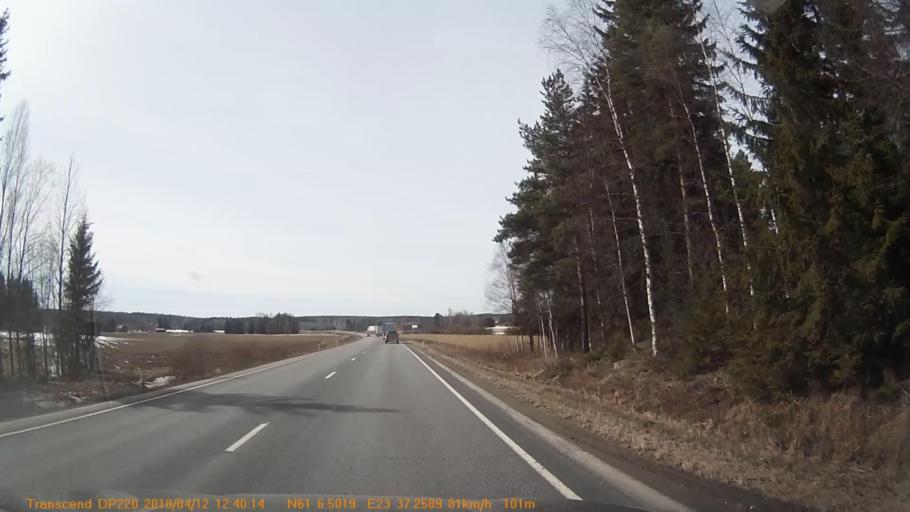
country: FI
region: Pirkanmaa
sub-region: Etelae-Pirkanmaa
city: Kylmaekoski
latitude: 61.1083
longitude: 23.6204
